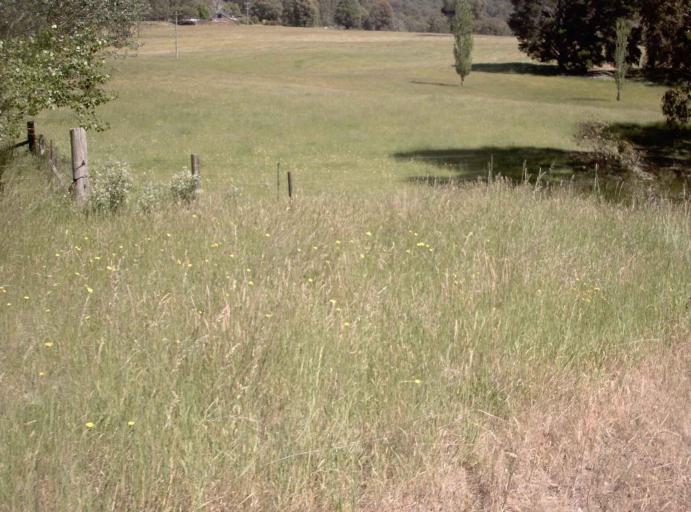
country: AU
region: New South Wales
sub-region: Bombala
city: Bombala
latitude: -37.0541
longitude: 148.8056
